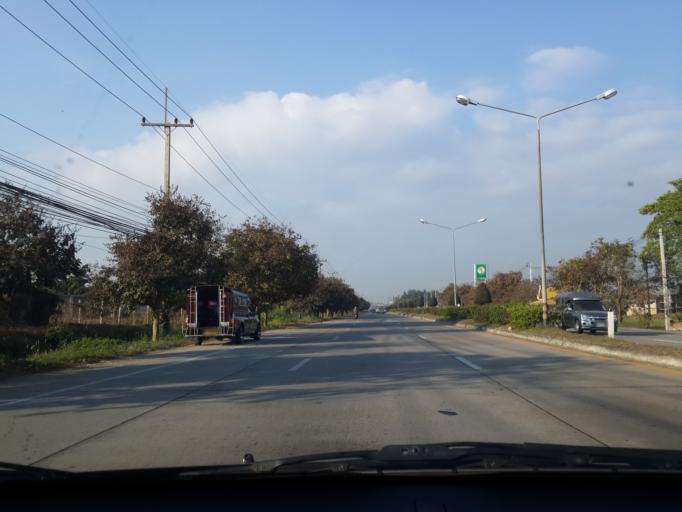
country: TH
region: Chiang Mai
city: San Sai
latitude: 18.8539
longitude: 99.0946
